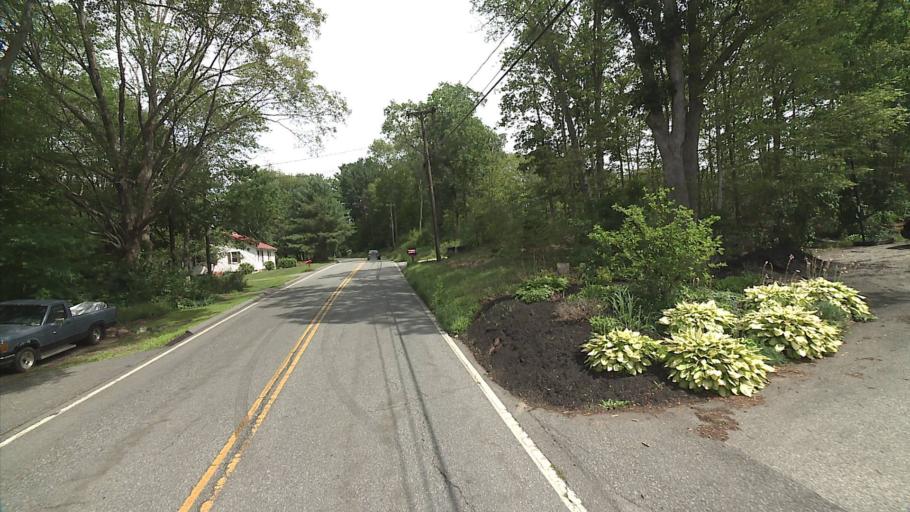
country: US
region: Connecticut
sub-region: Windham County
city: Killingly Center
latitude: 41.8822
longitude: -71.8694
